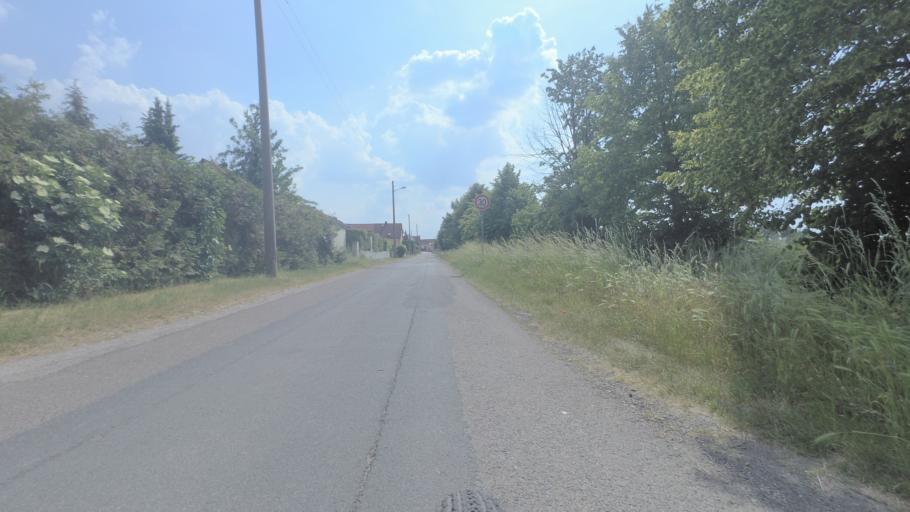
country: DE
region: Saxony-Anhalt
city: Koethen
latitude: 51.7636
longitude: 11.9309
